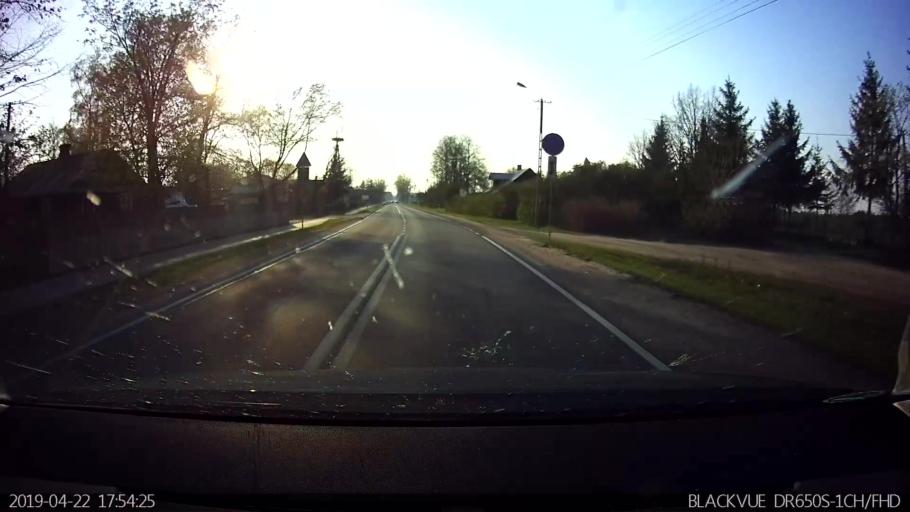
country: PL
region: Masovian Voivodeship
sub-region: Powiat wegrowski
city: Liw
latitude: 52.4571
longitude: 21.9399
